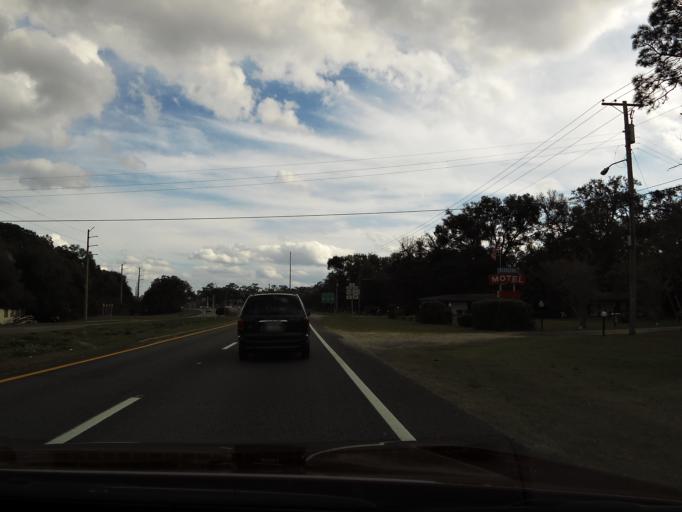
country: US
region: Florida
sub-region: Volusia County
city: De Leon Springs
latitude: 29.0902
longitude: -81.3283
